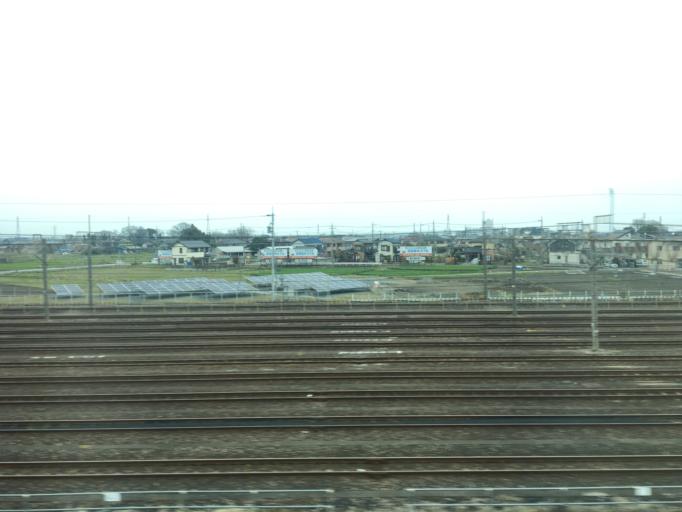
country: JP
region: Saitama
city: Kumagaya
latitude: 36.1595
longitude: 139.3578
